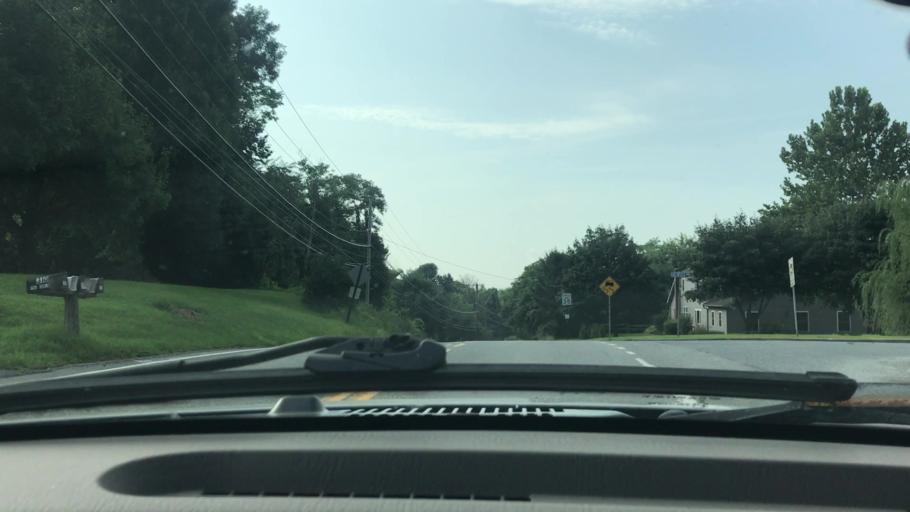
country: US
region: Pennsylvania
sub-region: Dauphin County
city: Middletown
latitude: 40.2177
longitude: -76.7430
